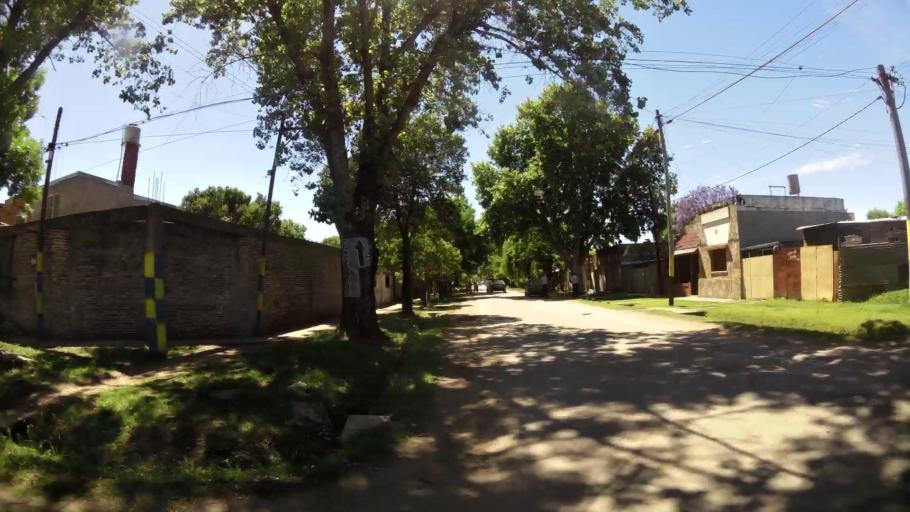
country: AR
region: Santa Fe
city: Perez
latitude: -32.9534
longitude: -60.7166
